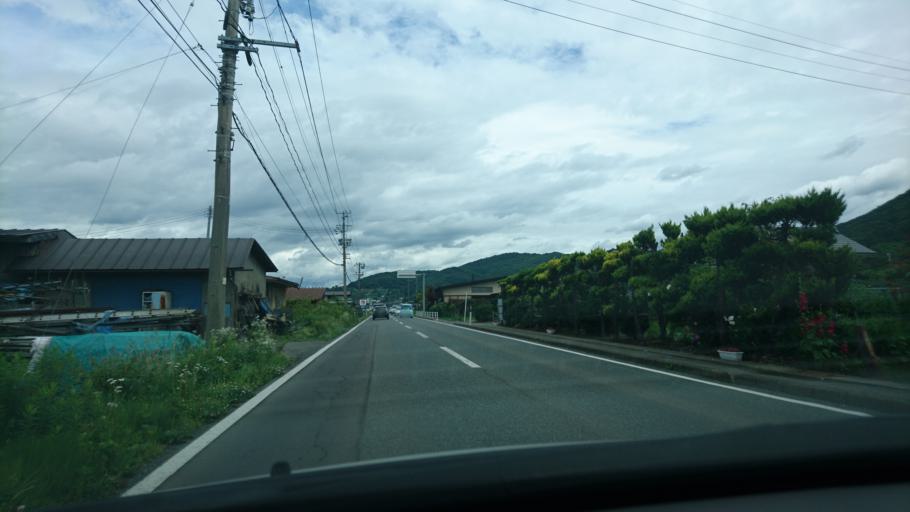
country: JP
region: Iwate
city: Morioka-shi
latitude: 39.6443
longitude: 141.1848
